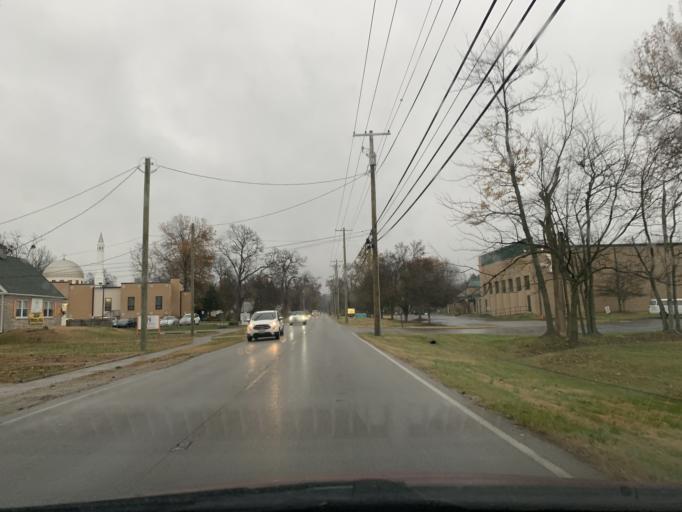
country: US
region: Kentucky
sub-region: Jefferson County
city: Buechel
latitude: 38.1959
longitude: -85.6508
